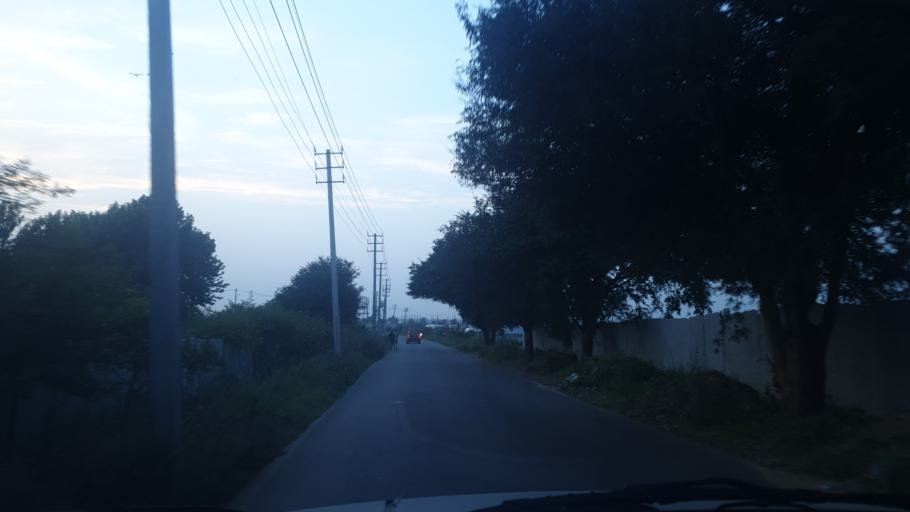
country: IN
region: Karnataka
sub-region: Bangalore Urban
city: Yelahanka
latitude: 13.0777
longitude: 77.6958
